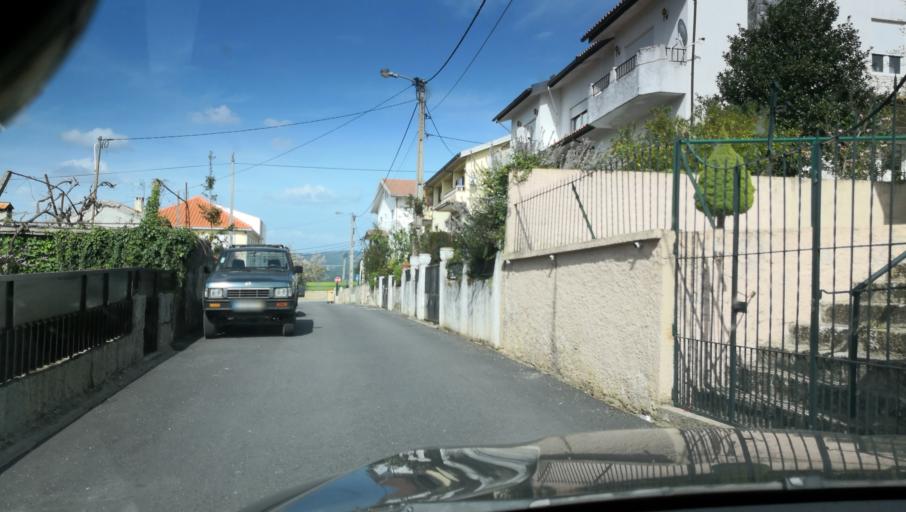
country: PT
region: Vila Real
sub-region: Vila Real
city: Vila Real
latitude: 41.2828
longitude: -7.7325
